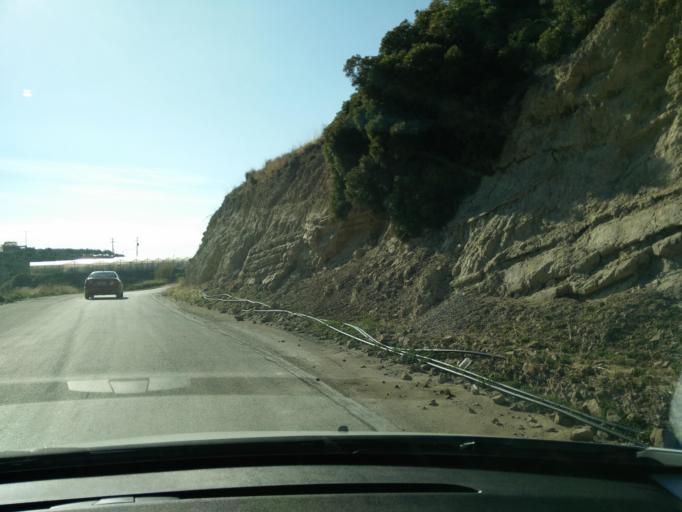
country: GR
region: Crete
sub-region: Nomos Lasithiou
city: Gra Liyia
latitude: 34.9959
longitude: 25.5290
